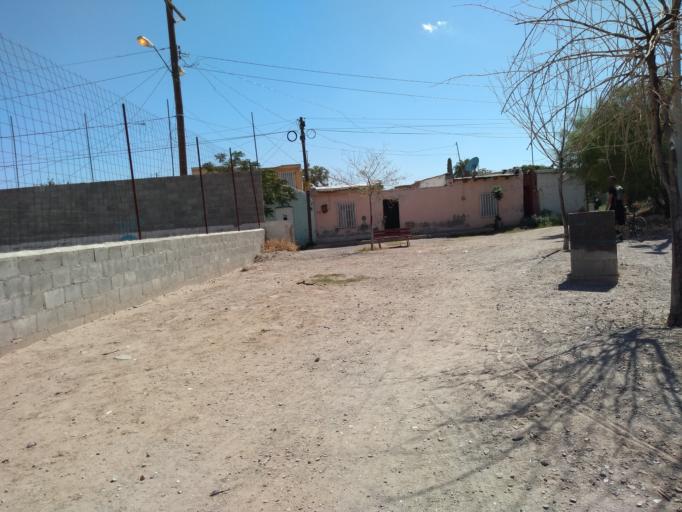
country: US
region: Texas
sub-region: El Paso County
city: El Paso
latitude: 31.7481
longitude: -106.4938
